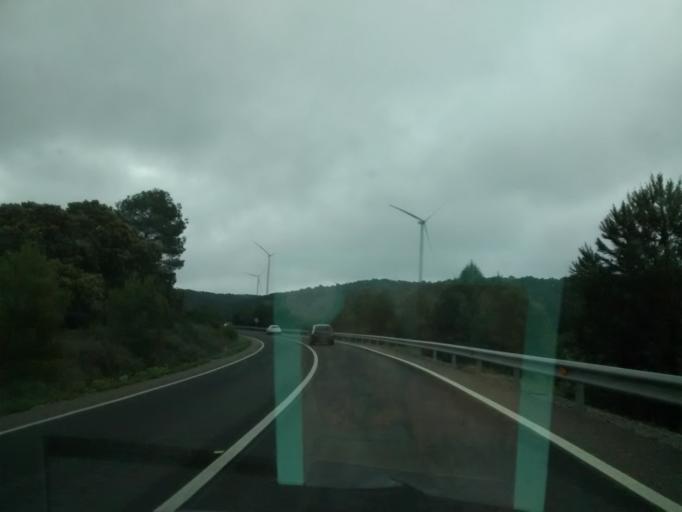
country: ES
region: Catalonia
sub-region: Provincia de Tarragona
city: Batea
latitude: 41.0637
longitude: 0.3370
